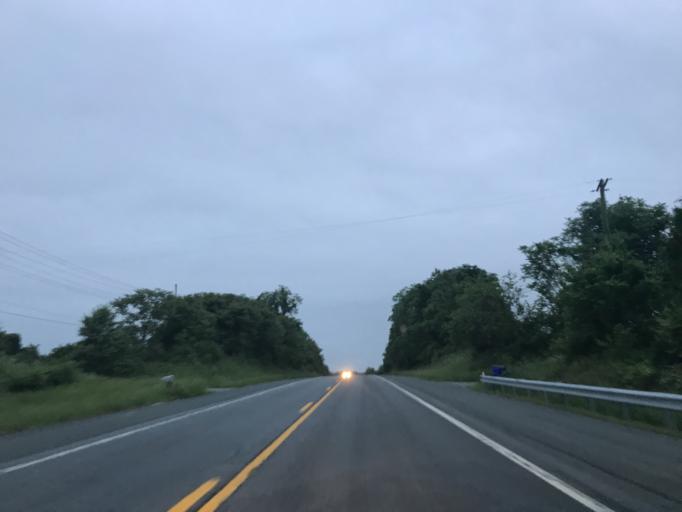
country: US
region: Maryland
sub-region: Frederick County
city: Linganore
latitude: 39.4004
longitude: -77.2598
